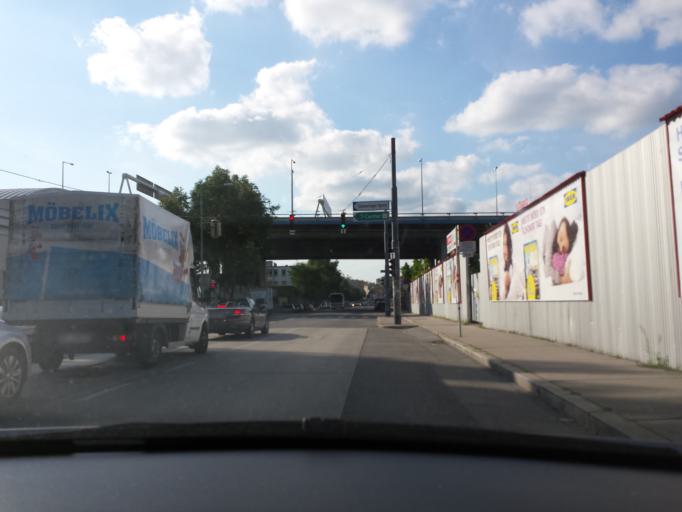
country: AT
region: Vienna
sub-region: Wien Stadt
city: Vienna
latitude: 48.1887
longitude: 16.4121
